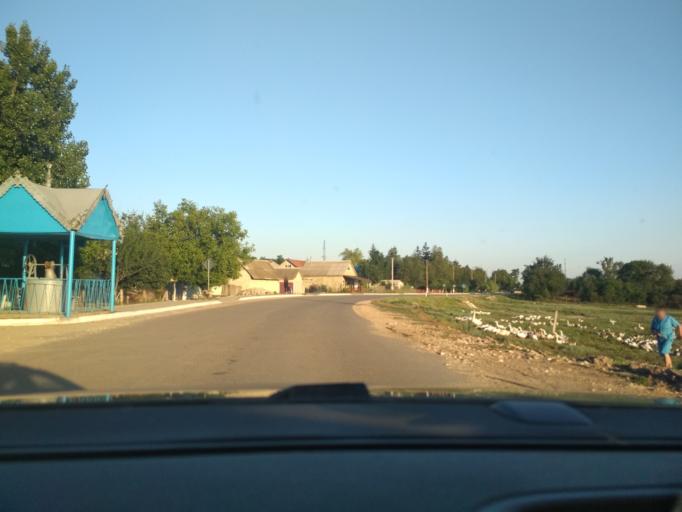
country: RO
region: Iasi
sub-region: Comuna Grozesti
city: Grozesti
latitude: 47.0106
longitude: 28.0735
